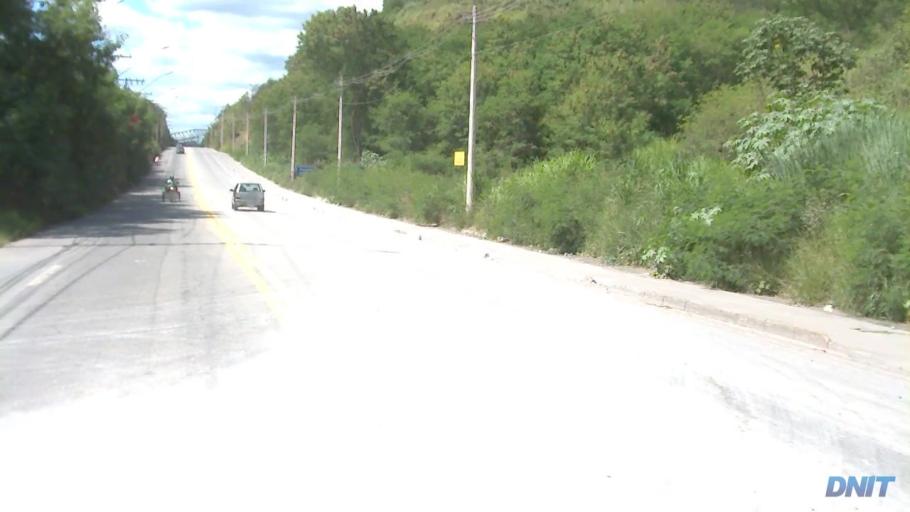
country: BR
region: Minas Gerais
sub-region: Coronel Fabriciano
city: Coronel Fabriciano
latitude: -19.5293
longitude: -42.6584
